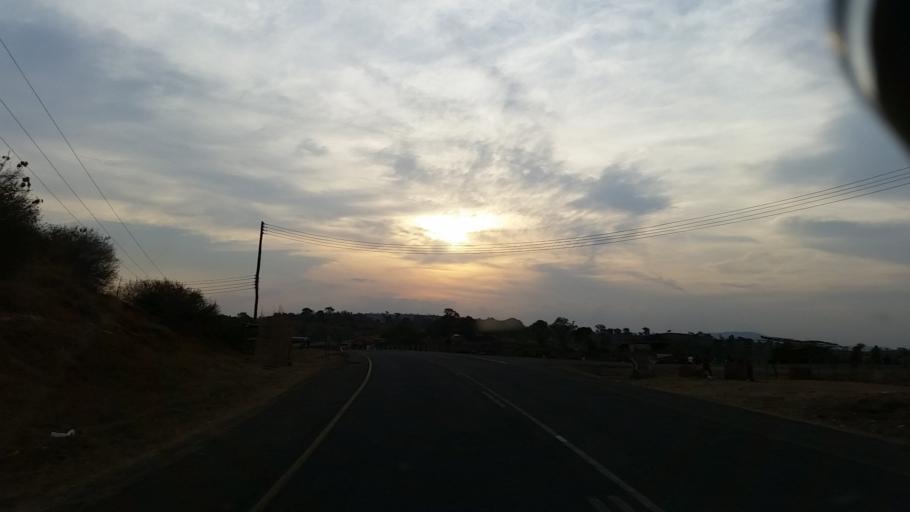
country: MW
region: Central Region
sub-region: Dowa District
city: Dowa
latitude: -13.7226
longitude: 34.0557
